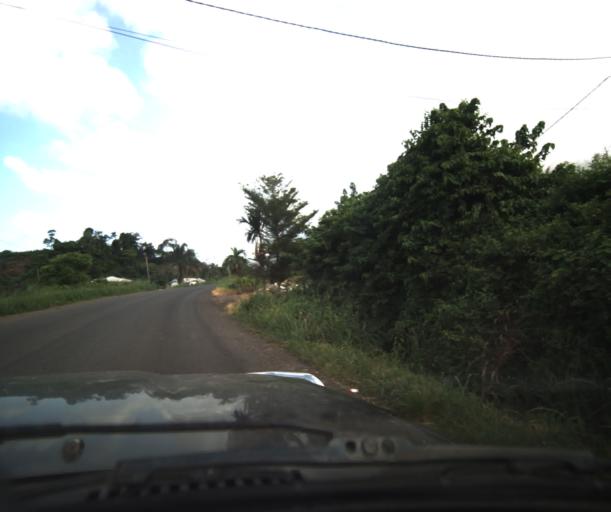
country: CM
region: South-West Province
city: Limbe
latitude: 4.0168
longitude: 9.1407
